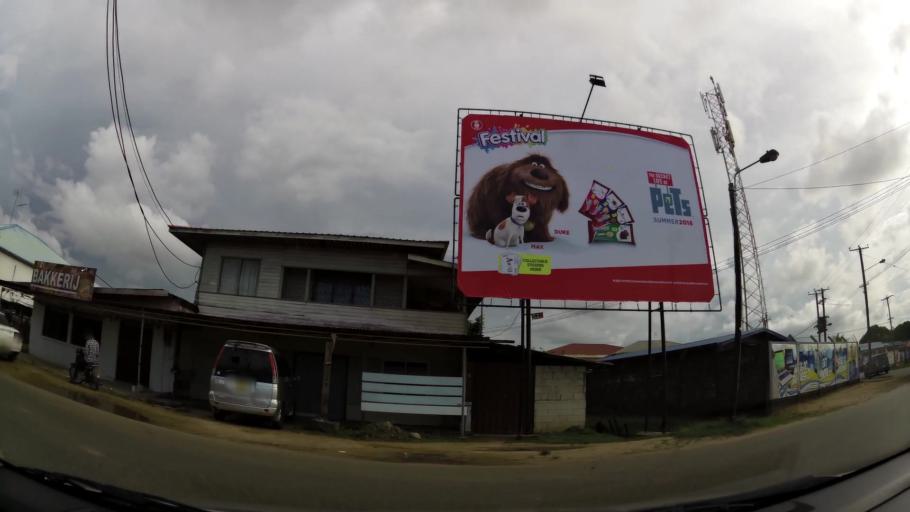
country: SR
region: Paramaribo
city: Paramaribo
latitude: 5.8477
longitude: -55.1837
